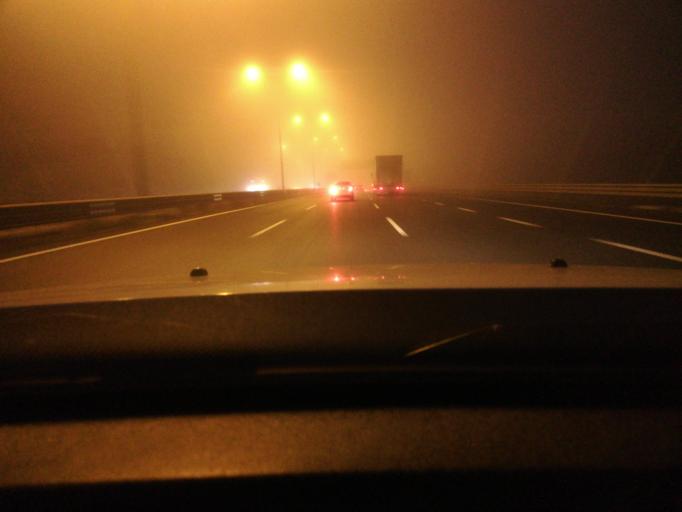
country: TR
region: Istanbul
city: Sultanbeyli
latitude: 40.9571
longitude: 29.3176
